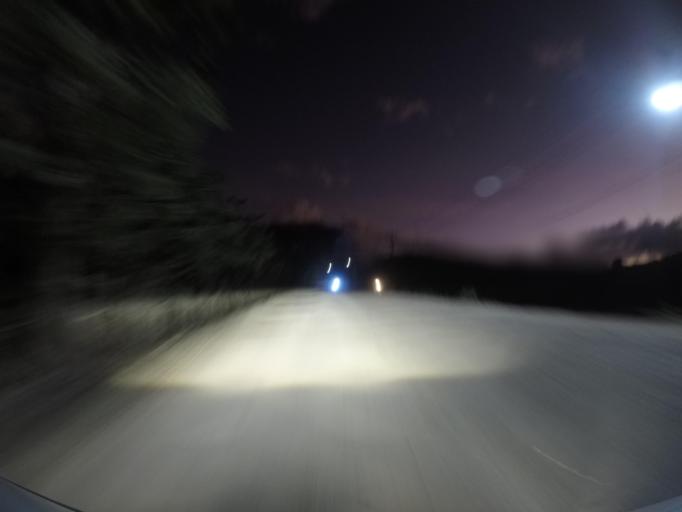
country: TL
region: Lautem
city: Lospalos
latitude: -8.4531
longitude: 127.0011
